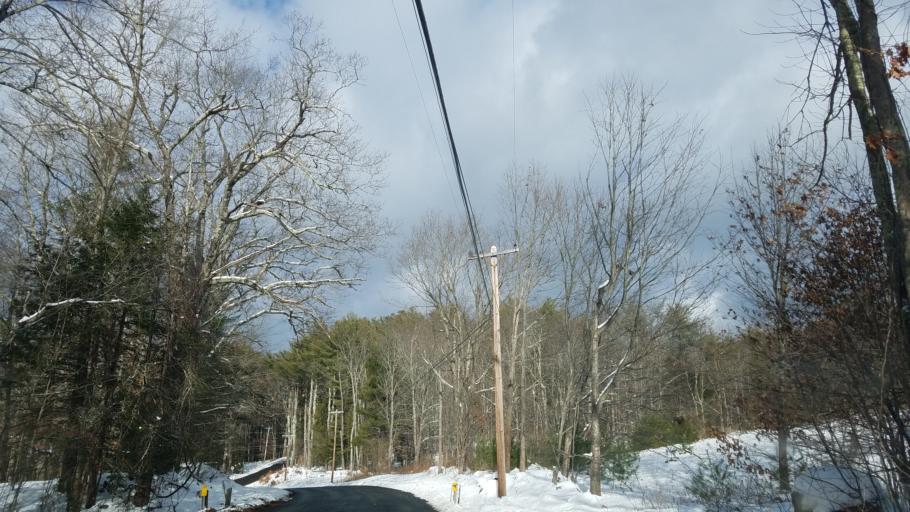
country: US
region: Connecticut
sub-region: Litchfield County
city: Winsted
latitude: 41.9715
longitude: -73.0364
